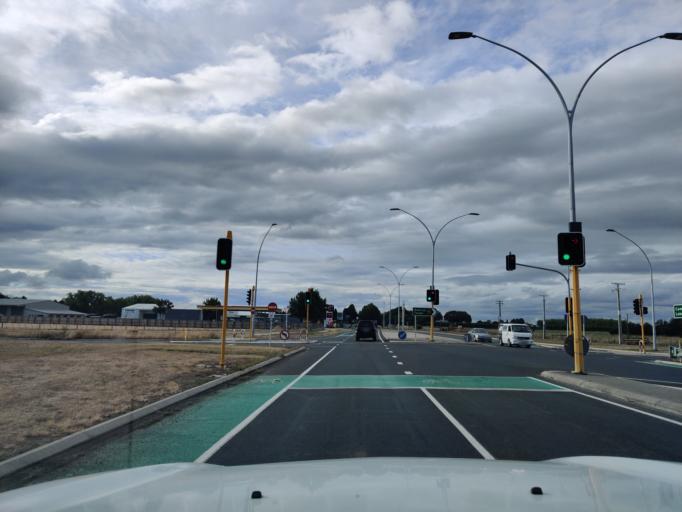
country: NZ
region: Waikato
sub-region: Waipa District
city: Cambridge
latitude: -37.8684
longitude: 175.4579
